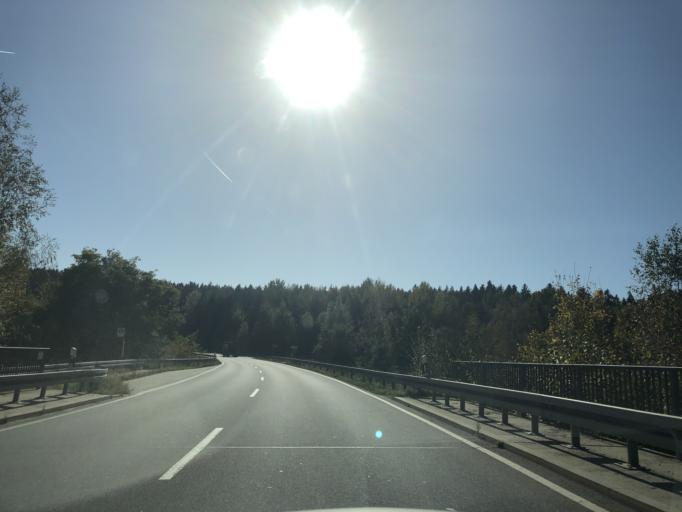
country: DE
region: Bavaria
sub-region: Lower Bavaria
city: Patersdorf
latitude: 49.0268
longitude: 12.9854
